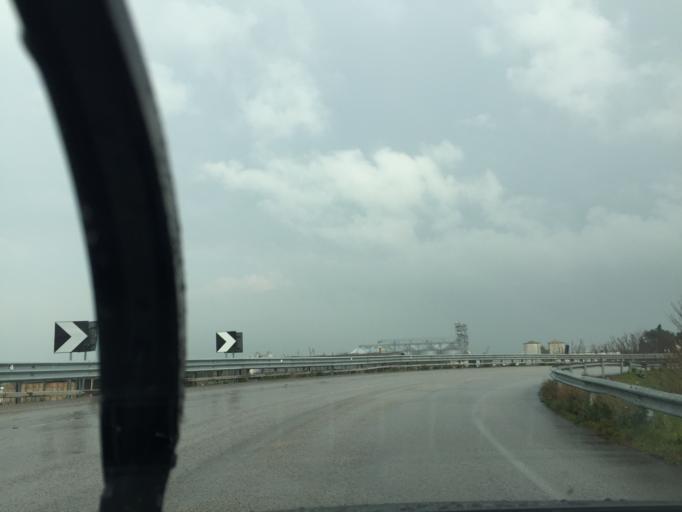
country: IT
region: Apulia
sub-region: Provincia di Foggia
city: Foggia
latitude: 41.4979
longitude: 15.5176
